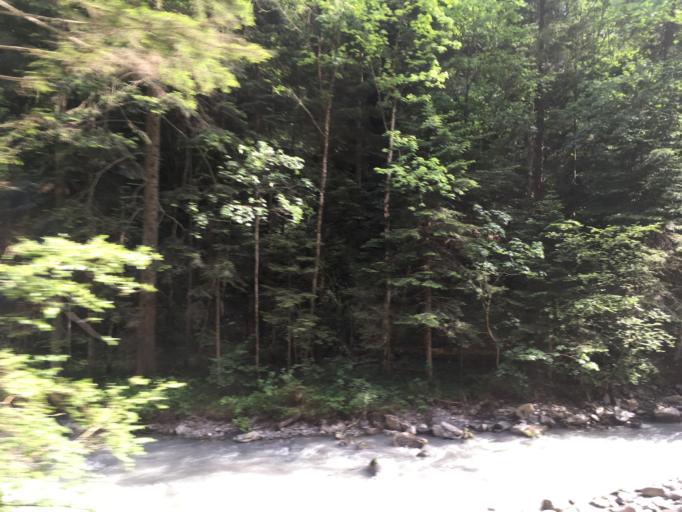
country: CH
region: Saint Gallen
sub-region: Wahlkreis Sarganserland
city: Bad Ragaz
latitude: 46.9841
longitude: 9.4896
